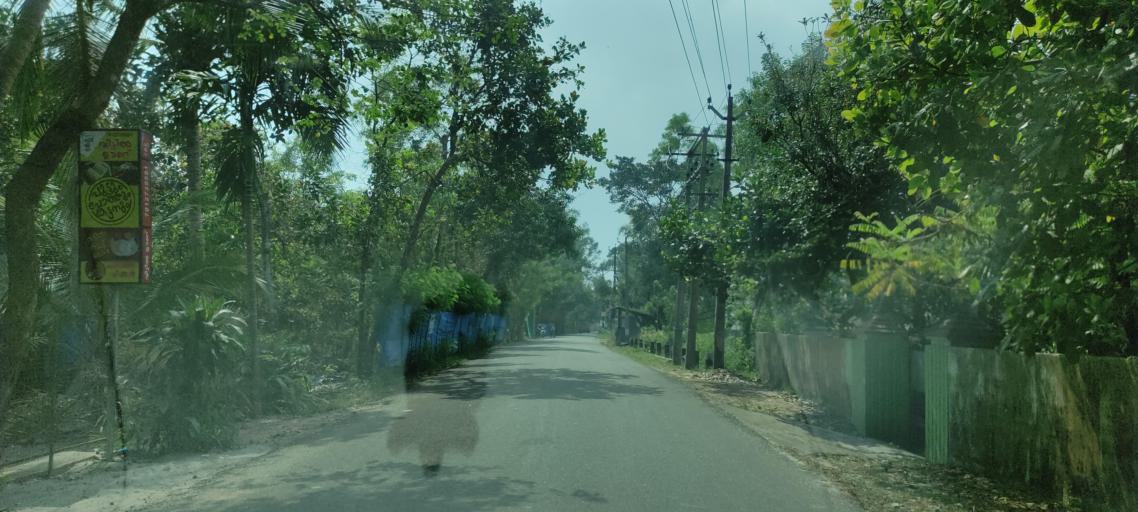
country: IN
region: Kerala
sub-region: Alappuzha
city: Shertallai
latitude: 9.6209
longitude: 76.3488
